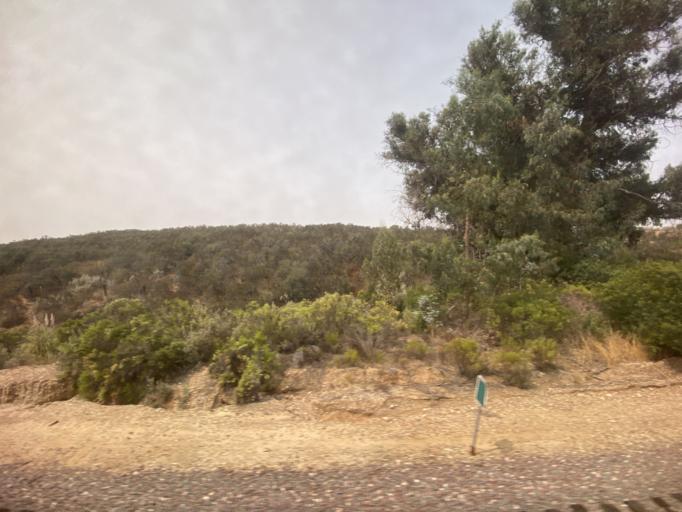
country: US
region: California
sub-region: San Diego County
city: La Jolla
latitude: 32.8749
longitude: -117.1751
